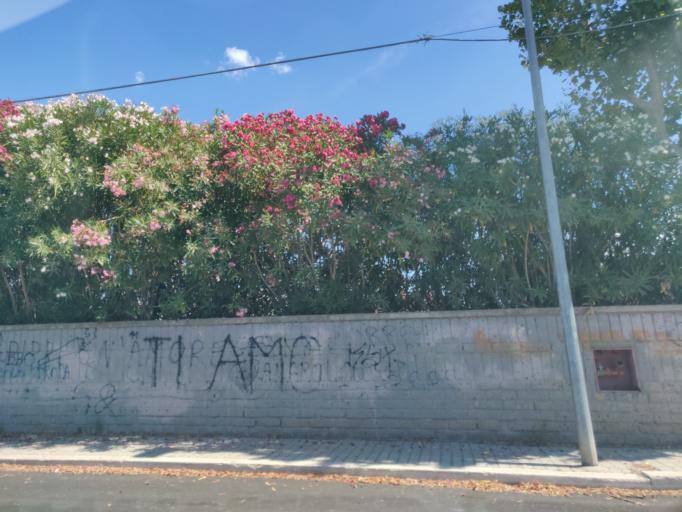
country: IT
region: Latium
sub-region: Citta metropolitana di Roma Capitale
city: Civitavecchia
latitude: 42.1026
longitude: 11.7977
